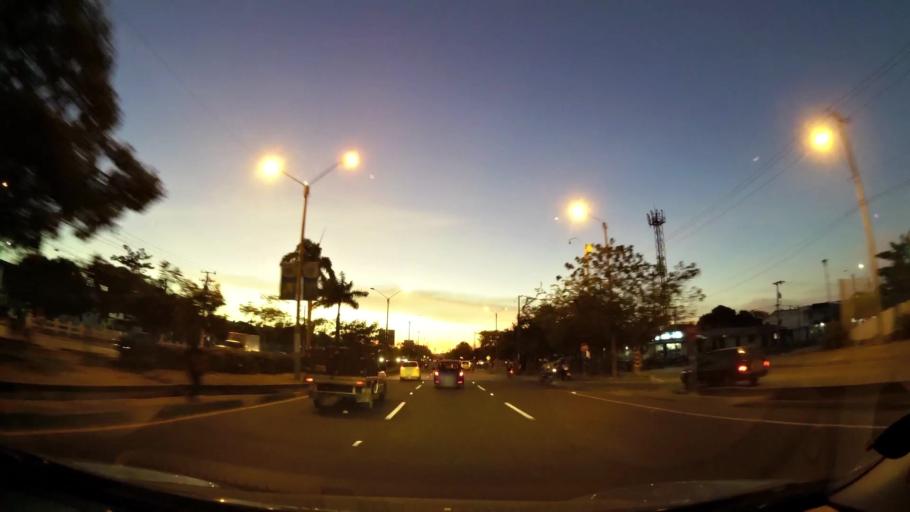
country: CO
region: Atlantico
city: Soledad
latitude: 10.9234
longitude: -74.8024
